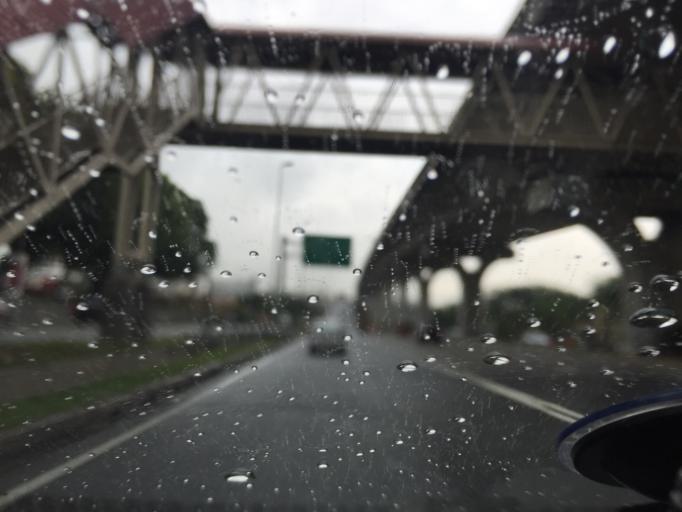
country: MY
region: Selangor
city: Subang Jaya
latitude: 3.0697
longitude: 101.5929
